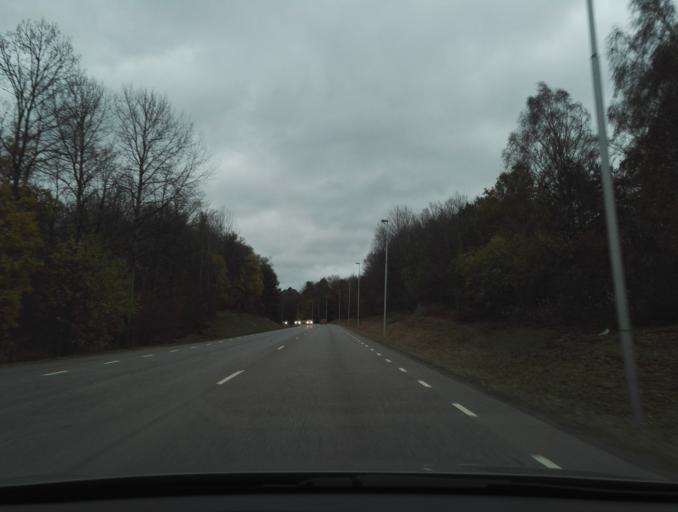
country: SE
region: Kronoberg
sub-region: Vaxjo Kommun
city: Vaexjoe
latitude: 56.8695
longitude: 14.7881
